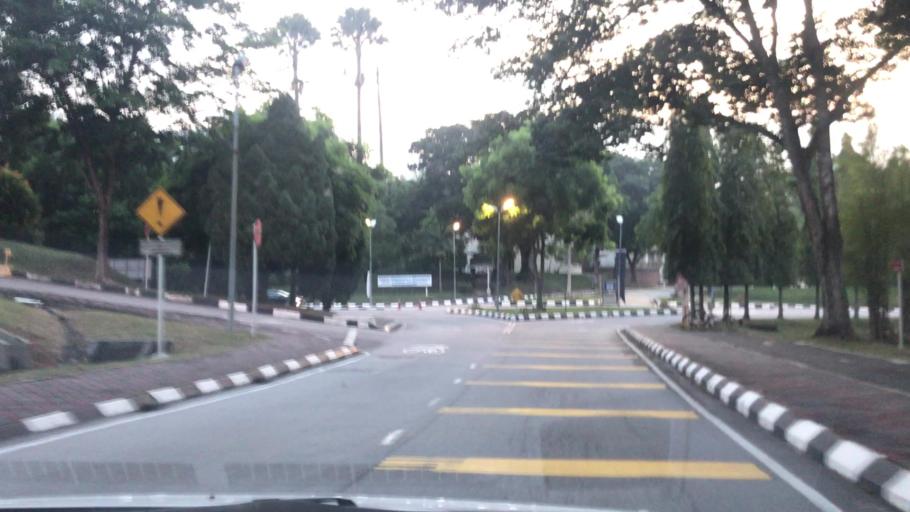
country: MY
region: Kuala Lumpur
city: Kuala Lumpur
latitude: 3.1192
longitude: 101.6551
